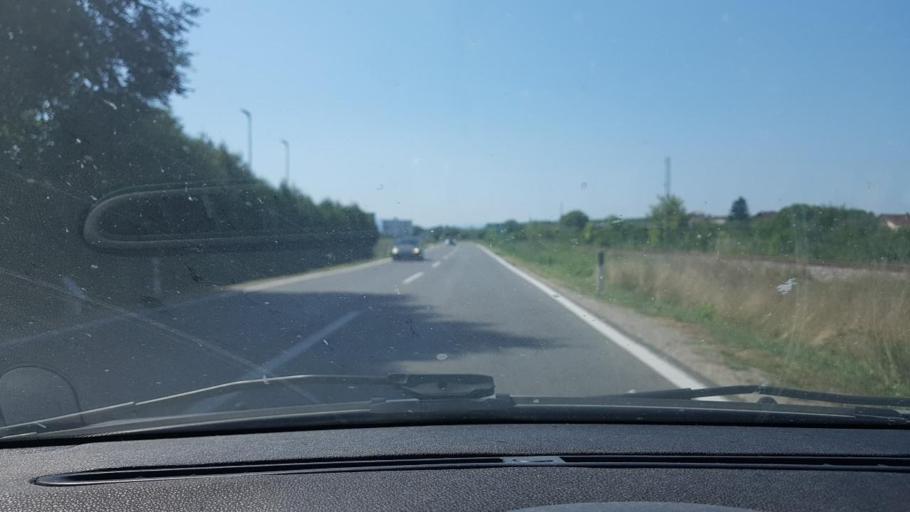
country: BA
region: Federation of Bosnia and Herzegovina
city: Bihac
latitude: 44.8023
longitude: 15.9059
